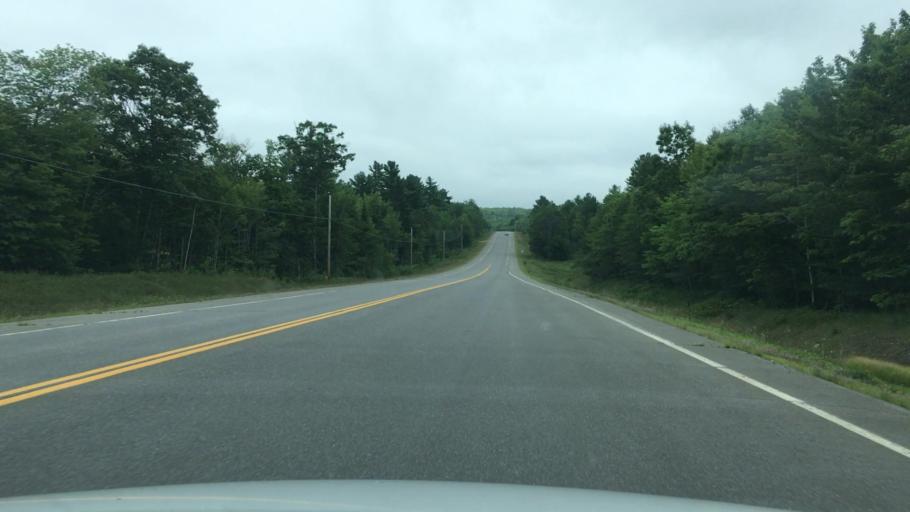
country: US
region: Maine
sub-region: Hancock County
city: Franklin
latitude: 44.8374
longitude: -68.1441
